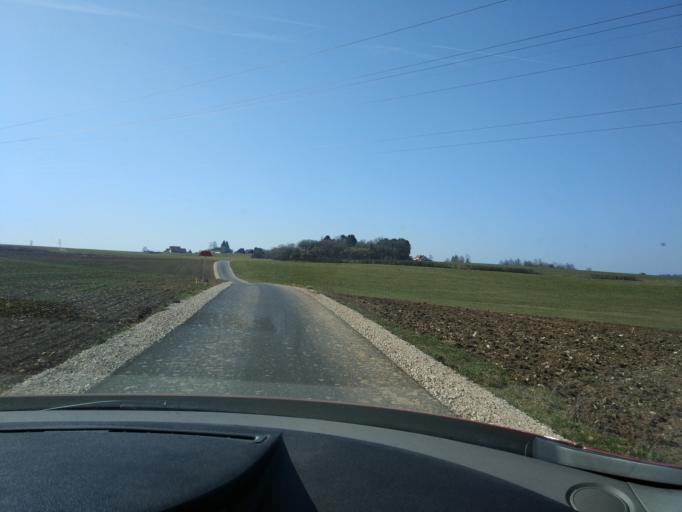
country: FR
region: Franche-Comte
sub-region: Departement du Doubs
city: Saone
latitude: 47.2298
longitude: 6.1341
